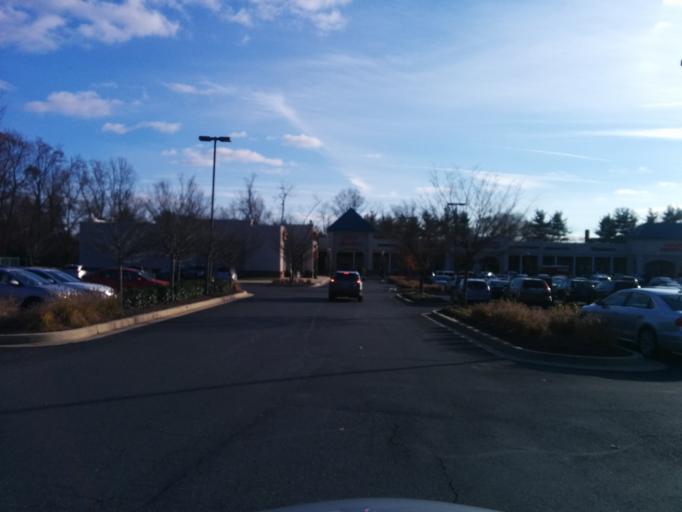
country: US
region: Maryland
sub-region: Montgomery County
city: Brookmont
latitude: 38.9503
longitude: -77.1184
